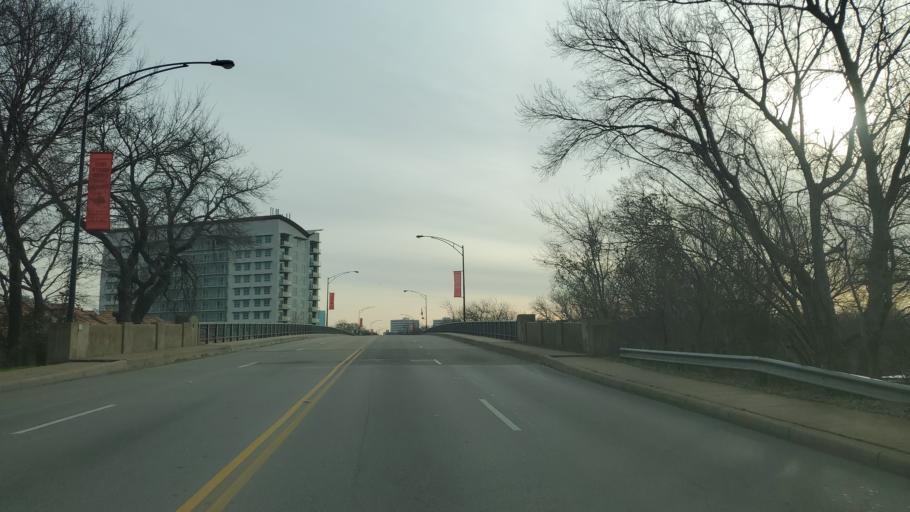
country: US
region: Texas
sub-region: Tarrant County
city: Fort Worth
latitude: 32.7473
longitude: -97.3560
